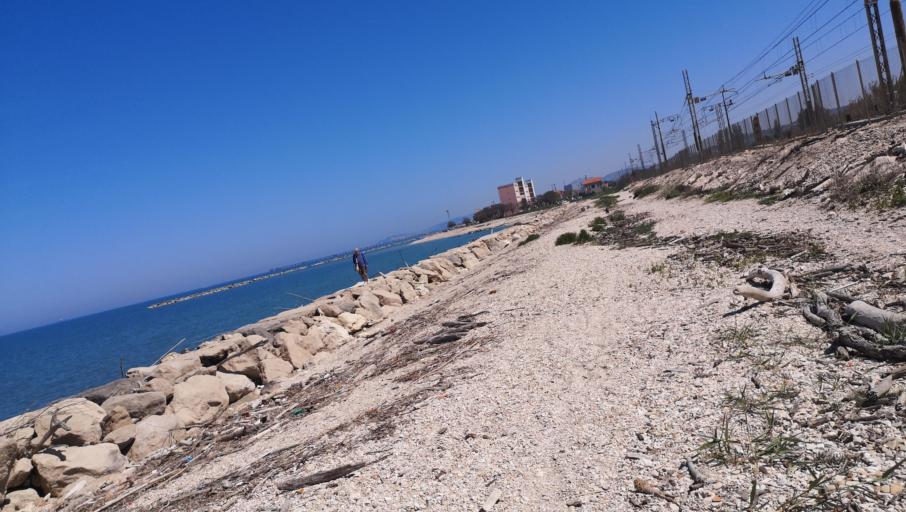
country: IT
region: The Marches
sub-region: Provincia di Ancona
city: Marina di Montemarciano
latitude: 43.6490
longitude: 13.3526
